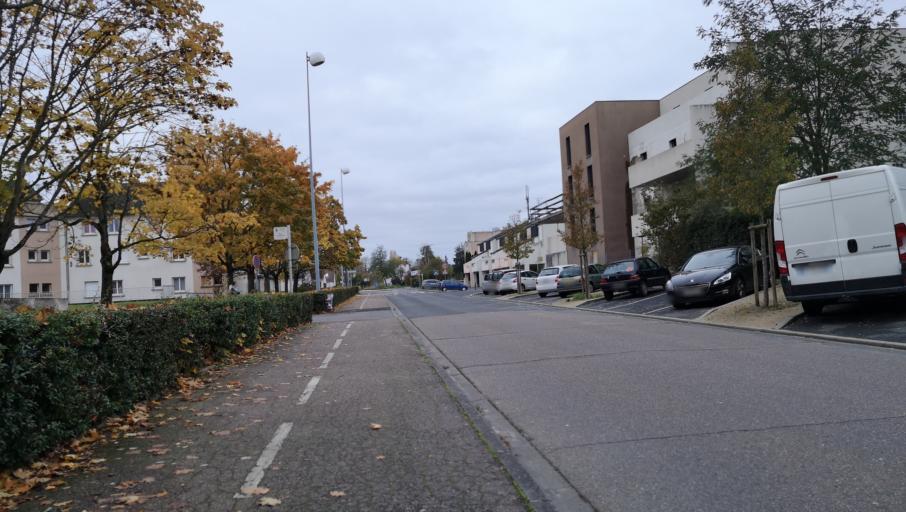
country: FR
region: Centre
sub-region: Departement du Loiret
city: Saint-Jean-de-Braye
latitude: 47.9140
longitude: 1.9676
